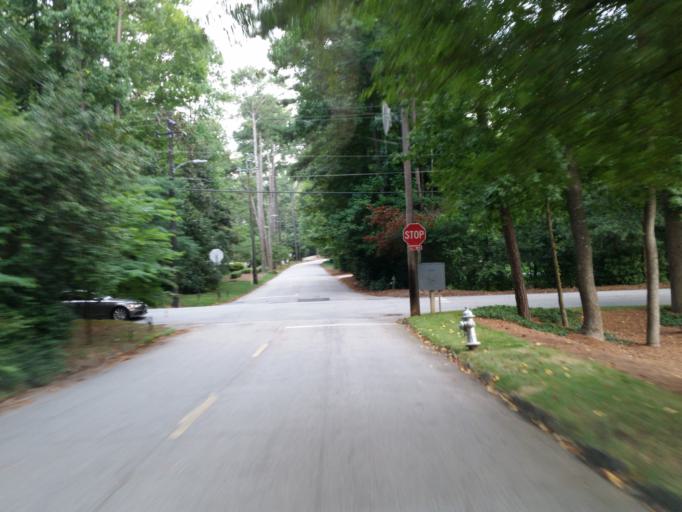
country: US
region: Georgia
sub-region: Cobb County
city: Vinings
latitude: 33.8452
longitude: -84.4417
